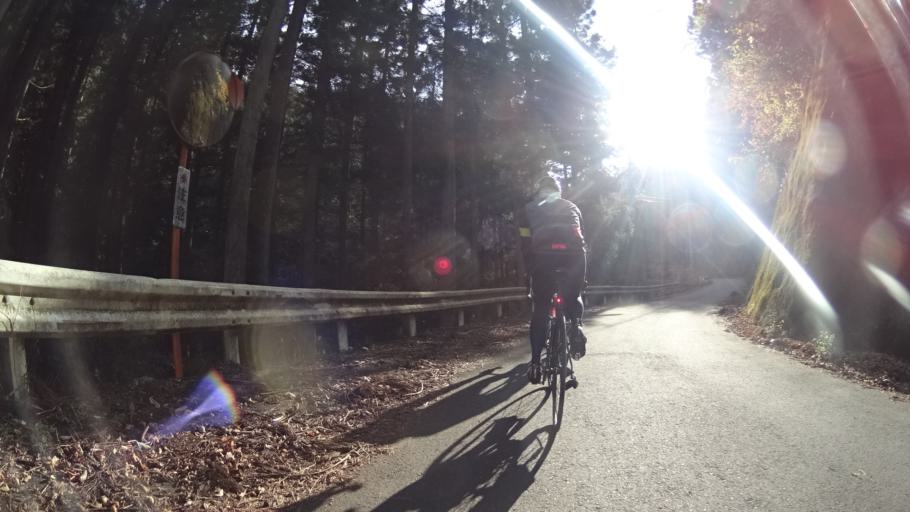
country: JP
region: Saitama
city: Chichibu
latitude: 35.9165
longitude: 139.1779
